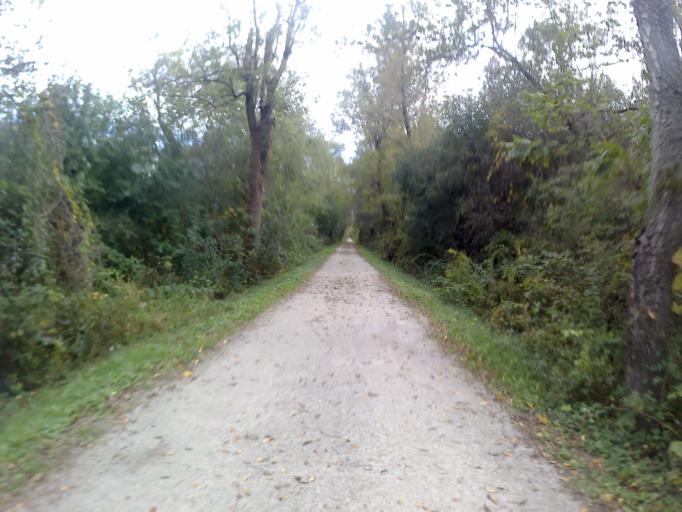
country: US
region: Illinois
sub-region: DuPage County
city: West Chicago
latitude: 41.8997
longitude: -88.1738
